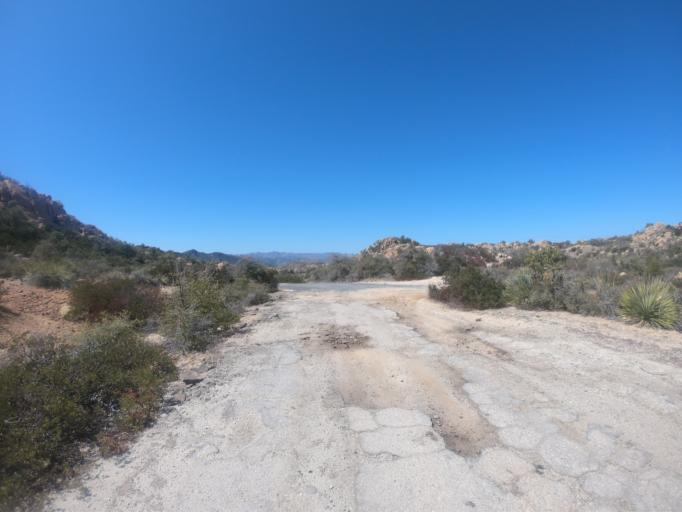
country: US
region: Arizona
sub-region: Gila County
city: Miami
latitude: 33.3549
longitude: -110.9671
